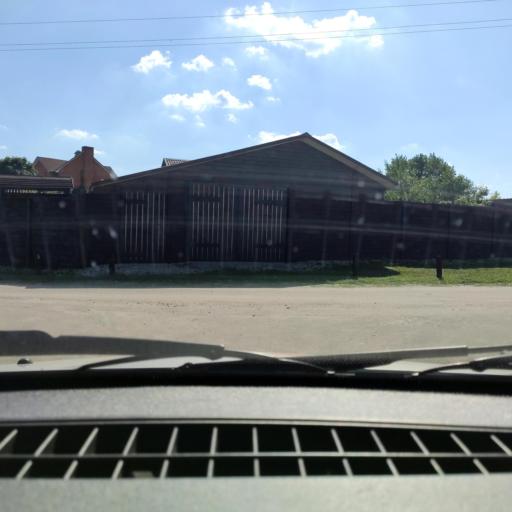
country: RU
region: Voronezj
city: Somovo
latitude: 51.8129
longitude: 39.2644
